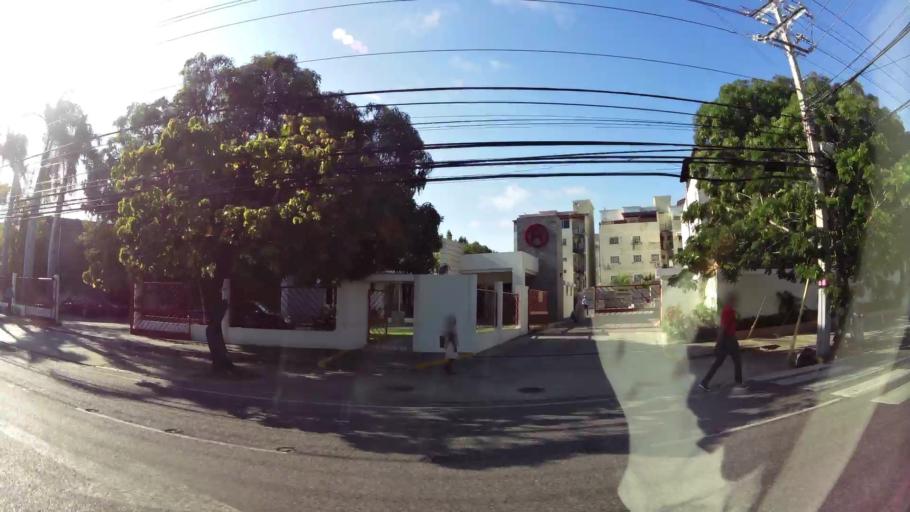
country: DO
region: Nacional
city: Bella Vista
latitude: 18.4462
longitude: -69.9341
